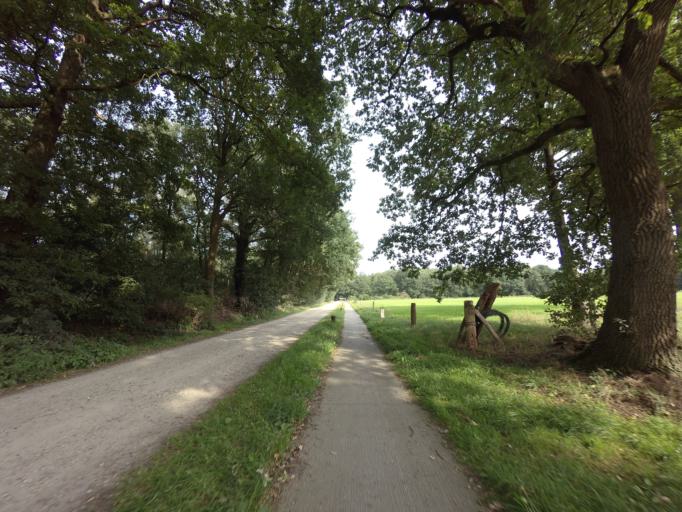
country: DE
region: Lower Saxony
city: Getelo
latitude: 52.4521
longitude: 6.8257
